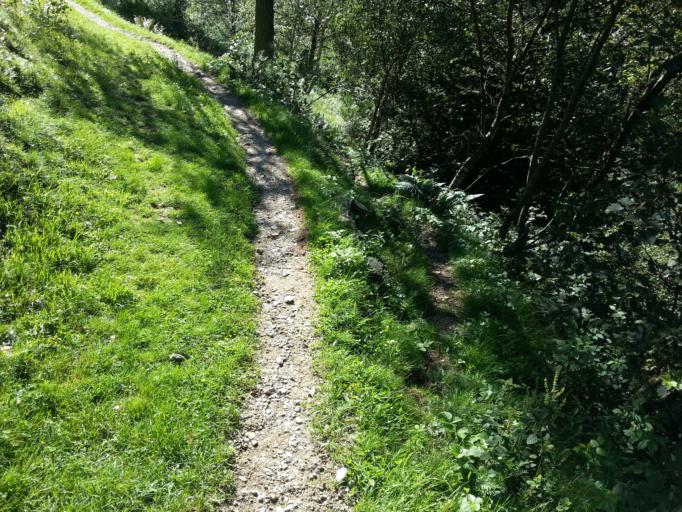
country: IT
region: Lombardy
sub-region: Provincia di Lecco
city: Premana
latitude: 46.0556
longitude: 9.4616
